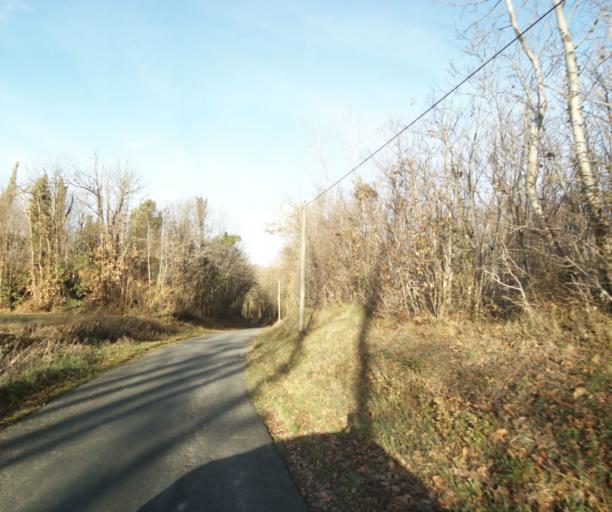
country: FR
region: Poitou-Charentes
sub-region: Departement de la Charente-Maritime
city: Ecoyeux
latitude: 45.7595
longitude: -0.4963
